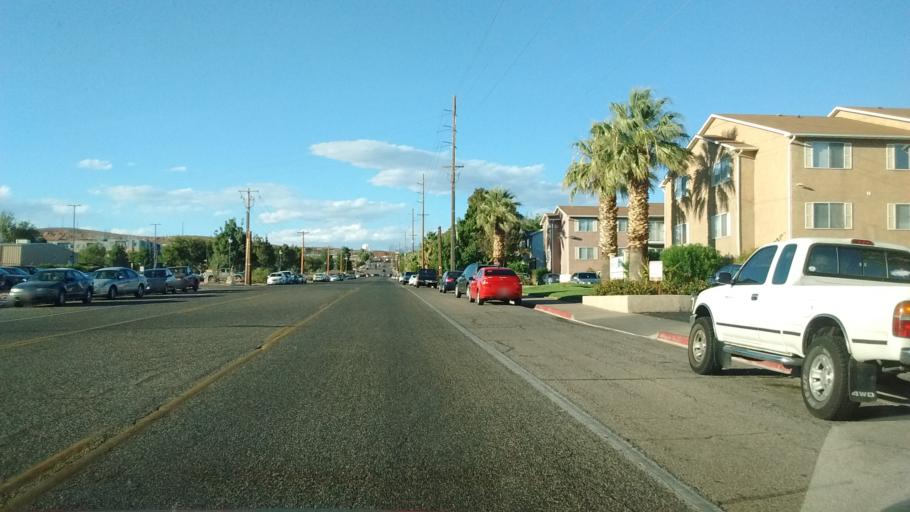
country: US
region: Utah
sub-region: Washington County
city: Saint George
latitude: 37.1023
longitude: -113.5621
